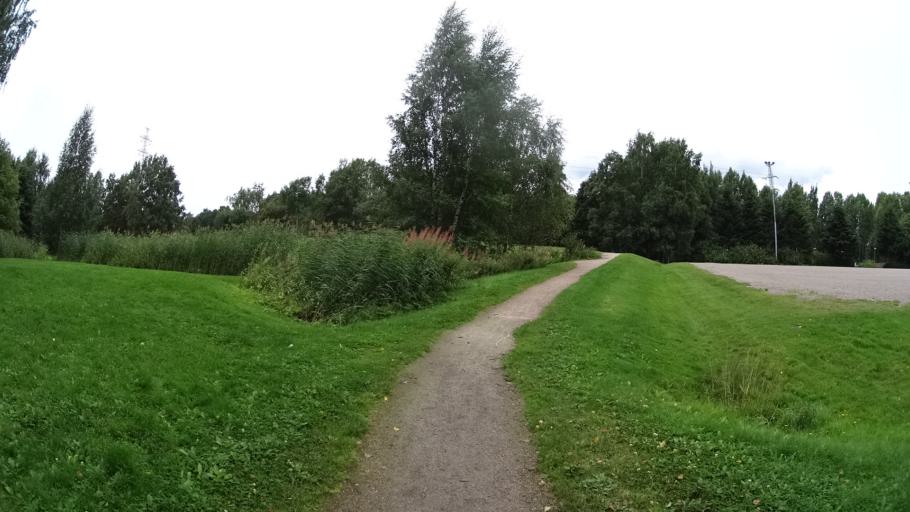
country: FI
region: Uusimaa
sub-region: Helsinki
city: Helsinki
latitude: 60.2028
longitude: 24.8904
